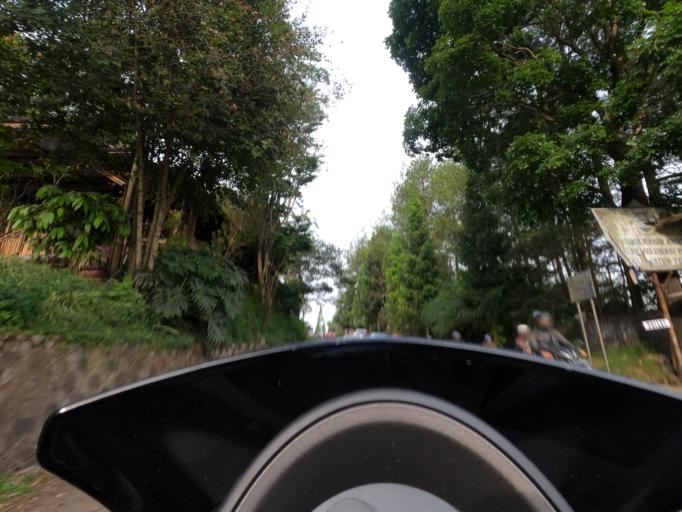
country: ID
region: West Java
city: Lembang
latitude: -6.8083
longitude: 107.6376
